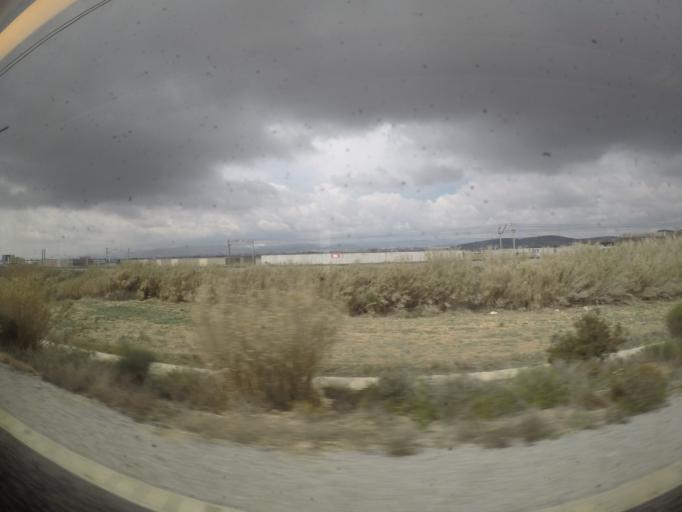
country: ES
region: Catalonia
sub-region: Provincia de Barcelona
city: Castellet
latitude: 41.3125
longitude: 1.6567
